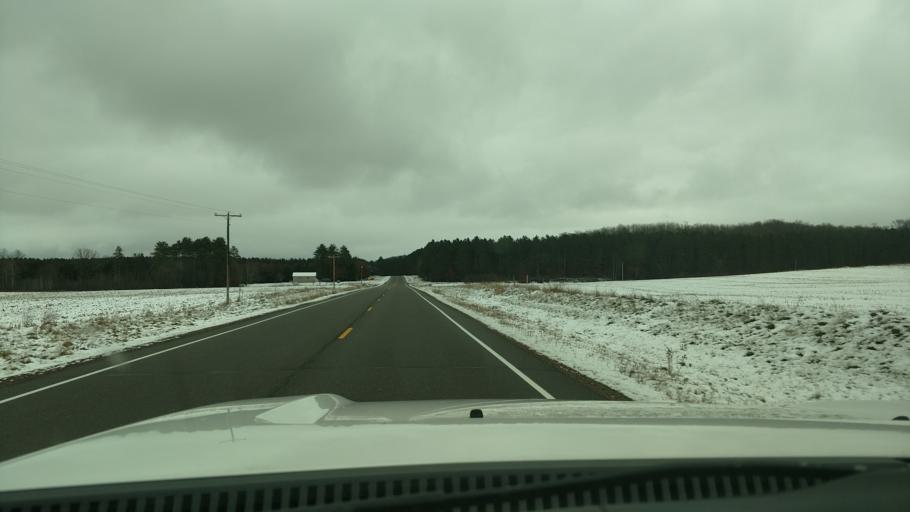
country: US
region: Wisconsin
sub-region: Dunn County
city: Colfax
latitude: 45.1390
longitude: -91.7521
